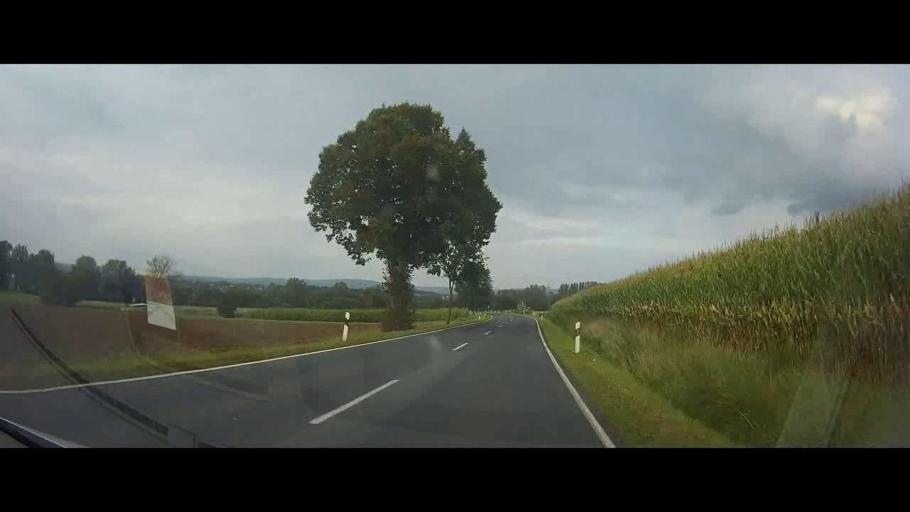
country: DE
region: Lower Saxony
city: Uslar
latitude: 51.6131
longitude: 9.6704
